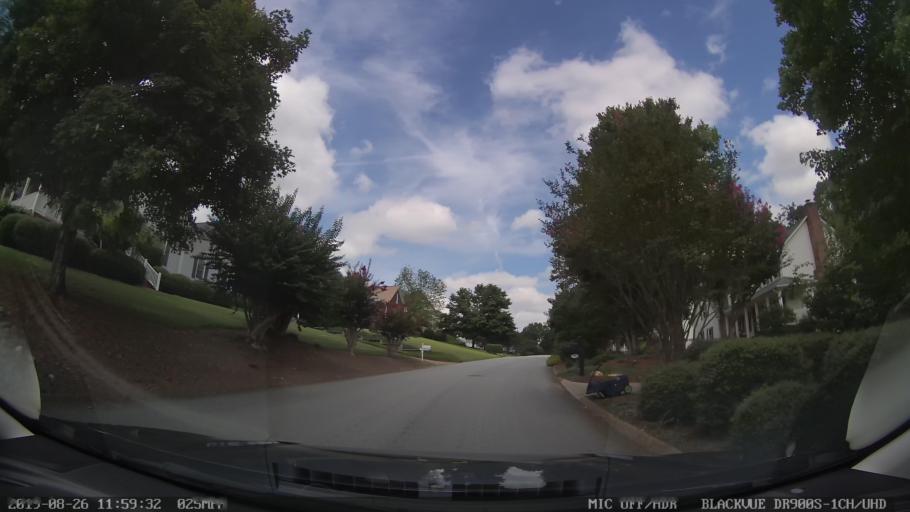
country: US
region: South Carolina
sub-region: Greenville County
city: Five Forks
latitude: 34.7964
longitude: -82.2339
